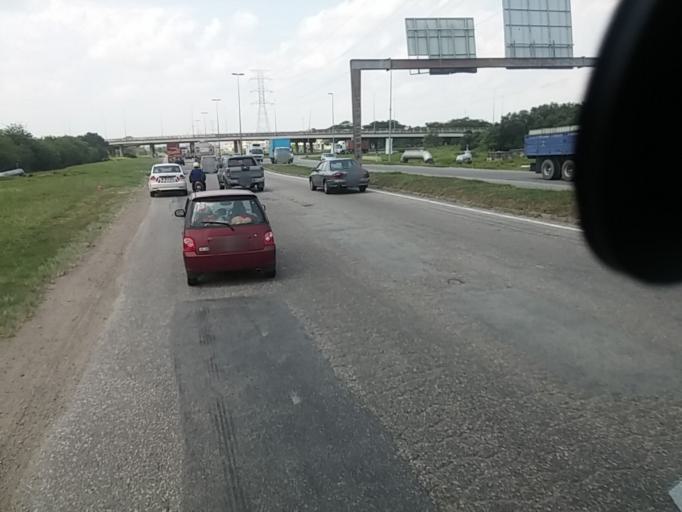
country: MY
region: Selangor
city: Klang
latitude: 2.9807
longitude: 101.4071
